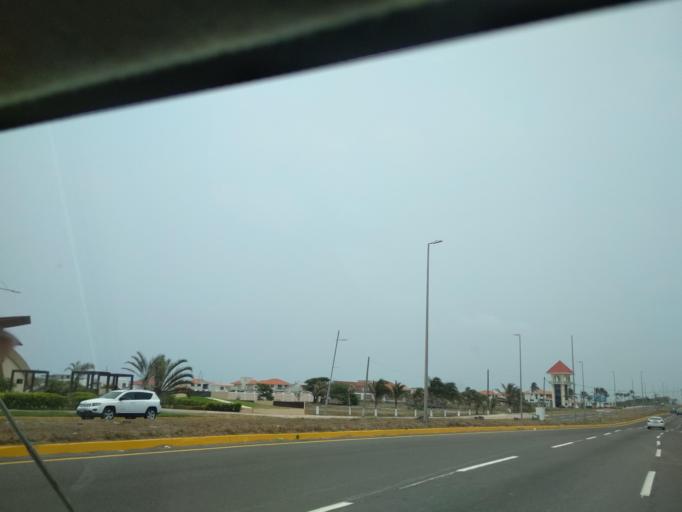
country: MX
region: Veracruz
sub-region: Alvarado
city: Playa de la Libertad
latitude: 19.0703
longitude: -96.0845
